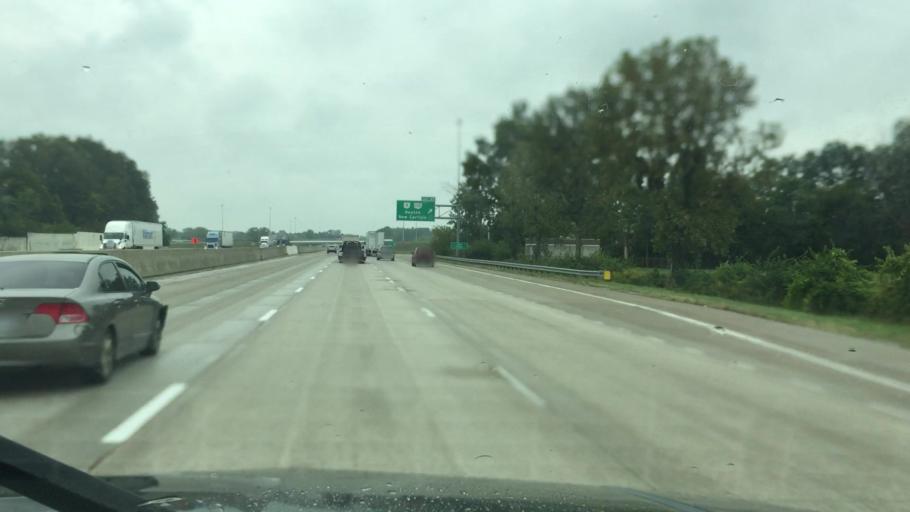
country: US
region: Ohio
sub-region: Clark County
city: Park Layne
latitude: 39.8652
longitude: -84.0471
